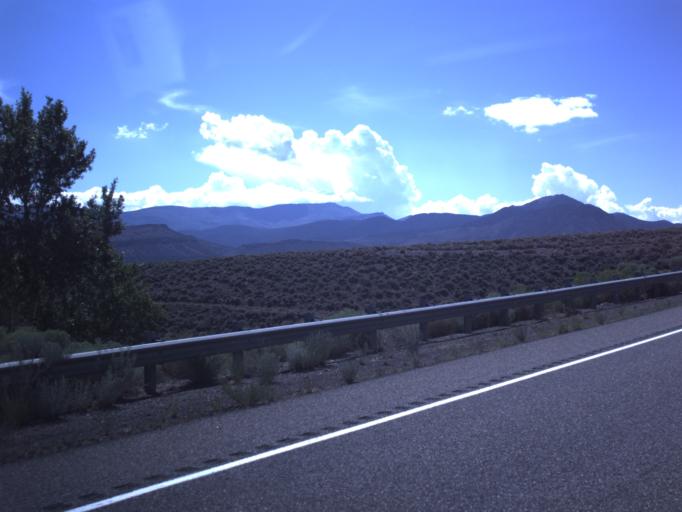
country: US
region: Utah
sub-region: Piute County
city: Junction
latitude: 38.3451
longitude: -112.2187
